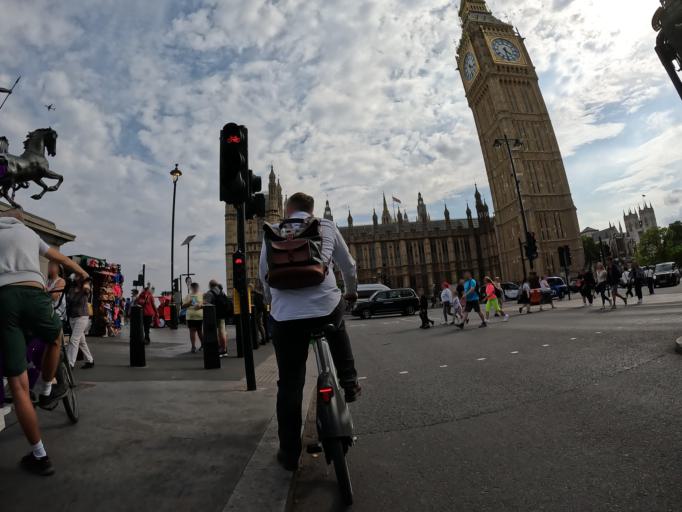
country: GB
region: England
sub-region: Kent
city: Halstead
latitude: 51.3434
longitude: 0.1211
